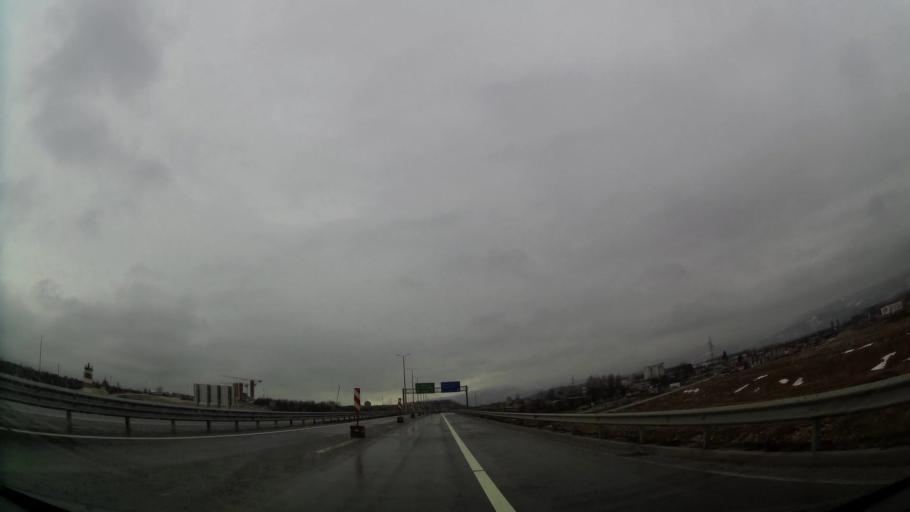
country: XK
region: Ferizaj
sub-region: Komuna e Kacanikut
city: Kacanik
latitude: 42.2809
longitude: 21.2101
